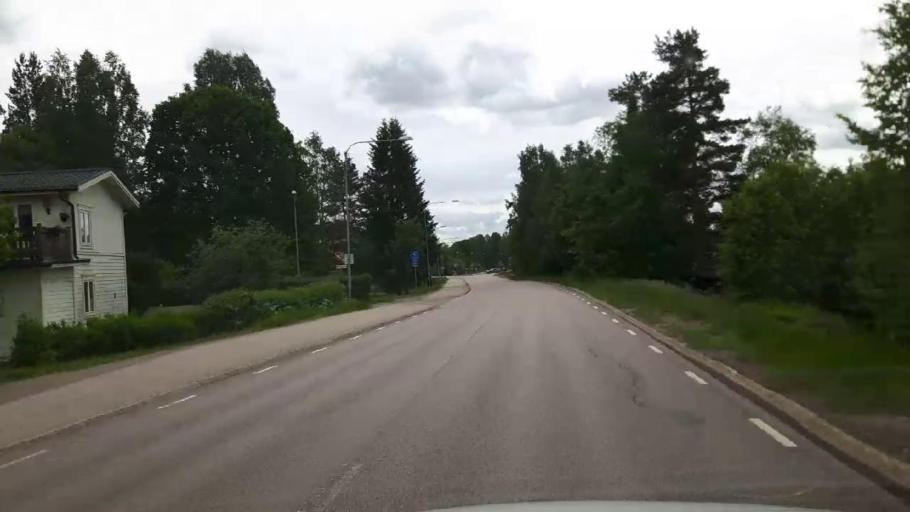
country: SE
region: Vaestmanland
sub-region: Norbergs Kommun
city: Norberg
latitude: 60.0762
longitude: 15.9302
